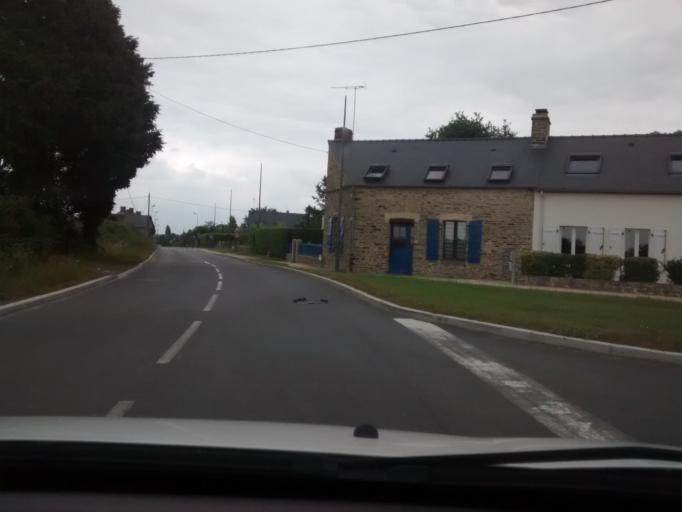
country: FR
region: Brittany
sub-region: Departement d'Ille-et-Vilaine
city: La Bouexiere
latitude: 48.1752
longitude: -1.4356
